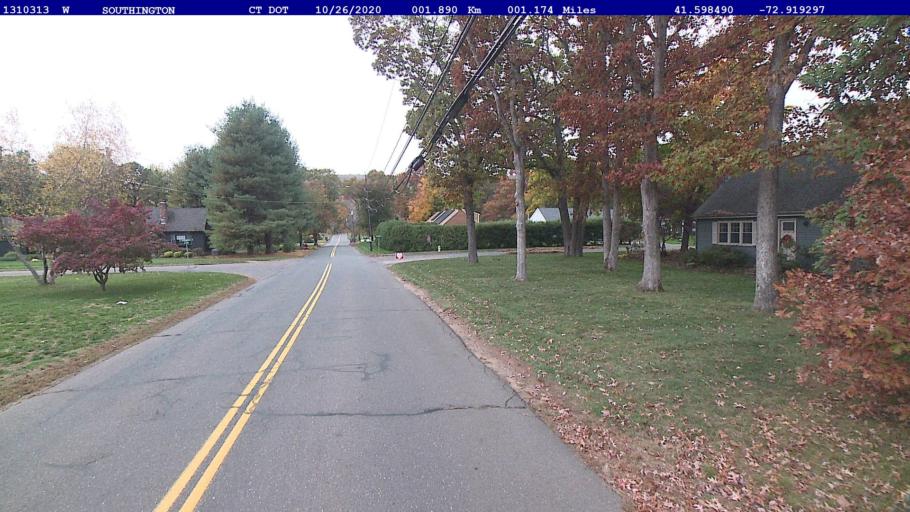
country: US
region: Connecticut
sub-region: New Haven County
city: Wolcott
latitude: 41.5985
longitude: -72.9193
